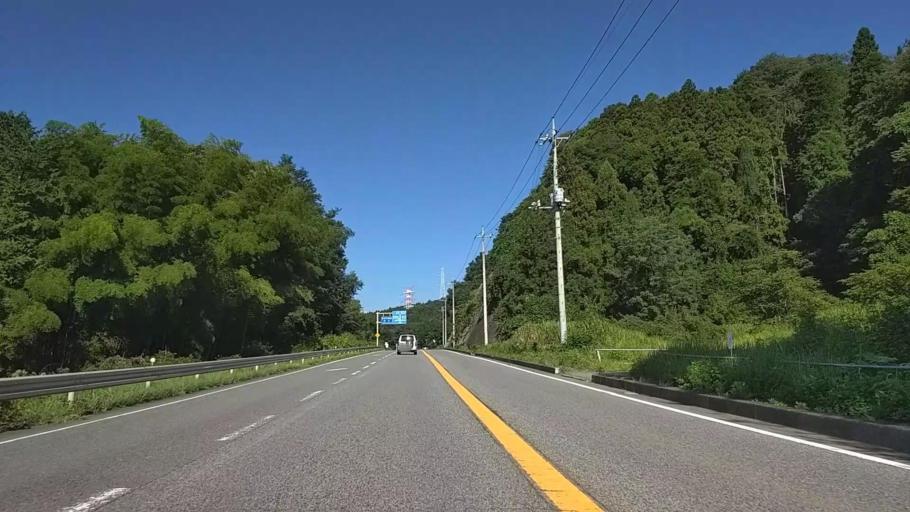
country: JP
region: Gunma
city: Annaka
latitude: 36.3193
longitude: 138.7933
